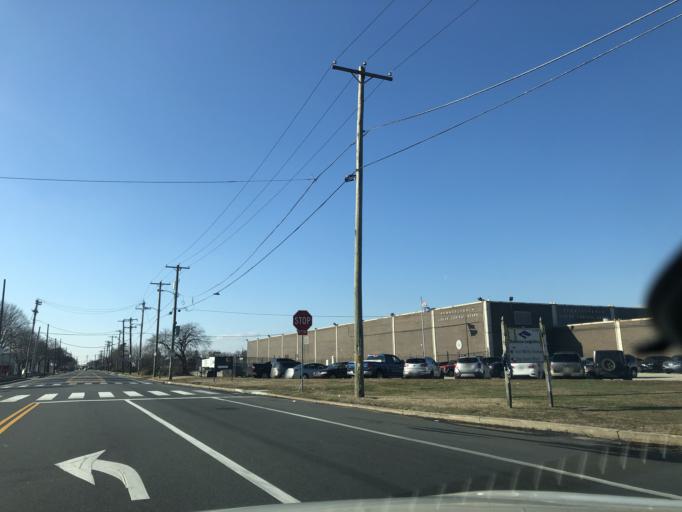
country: US
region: Pennsylvania
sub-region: Delaware County
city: Colwyn
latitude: 39.8840
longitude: -75.2229
